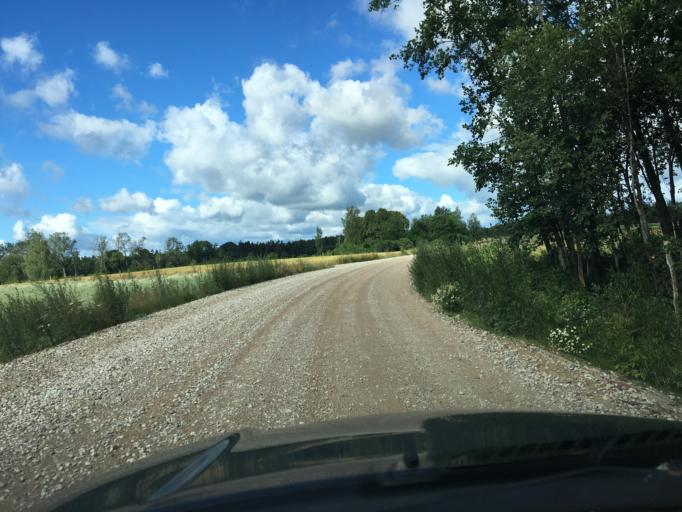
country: LV
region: Kuldigas Rajons
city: Kuldiga
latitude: 56.8382
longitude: 21.9208
